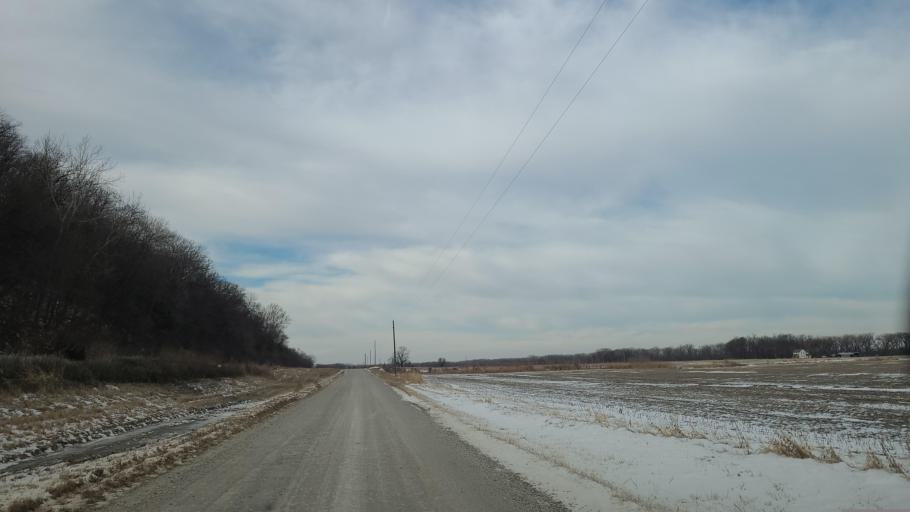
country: US
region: Kansas
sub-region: Jefferson County
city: Oskaloosa
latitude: 39.0612
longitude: -95.4400
